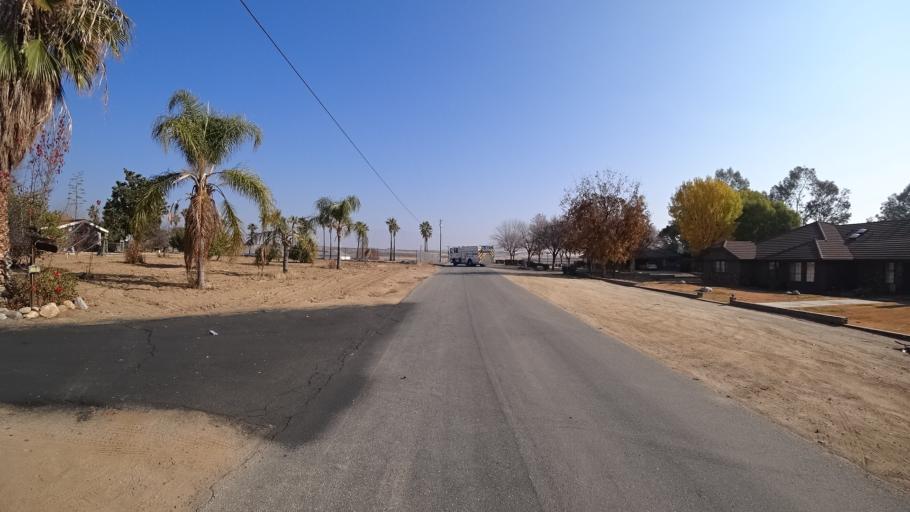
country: US
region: California
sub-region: Kern County
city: Oildale
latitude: 35.4144
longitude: -118.8818
